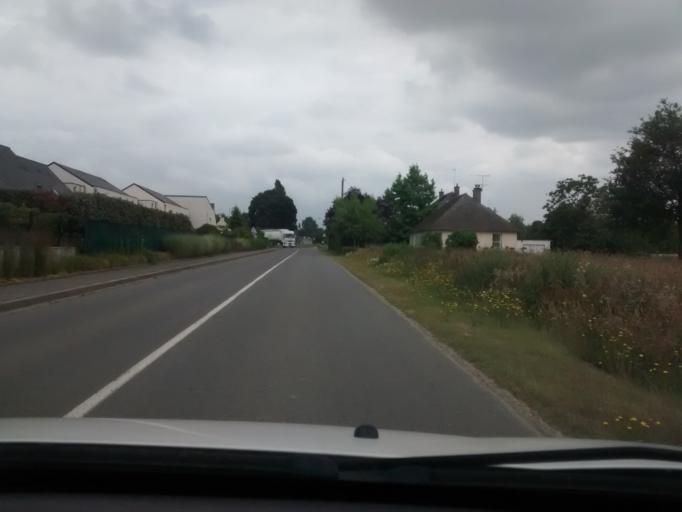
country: FR
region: Brittany
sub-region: Departement d'Ille-et-Vilaine
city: Liffre
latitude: 48.2043
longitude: -1.5099
